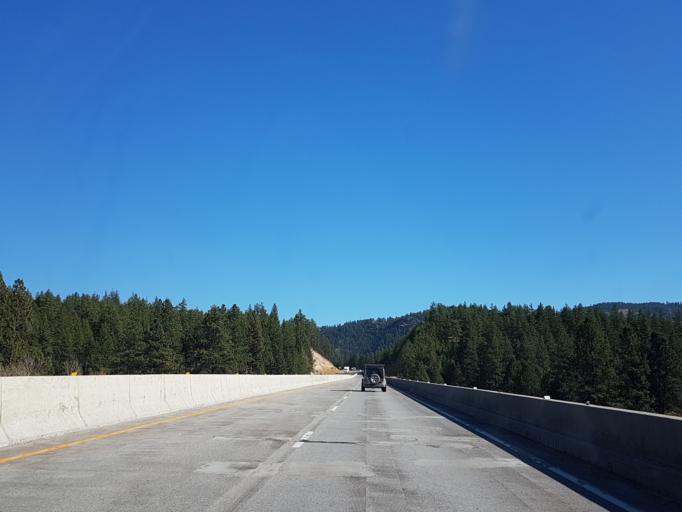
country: US
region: Montana
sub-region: Missoula County
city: Frenchtown
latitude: 47.0222
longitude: -114.3842
